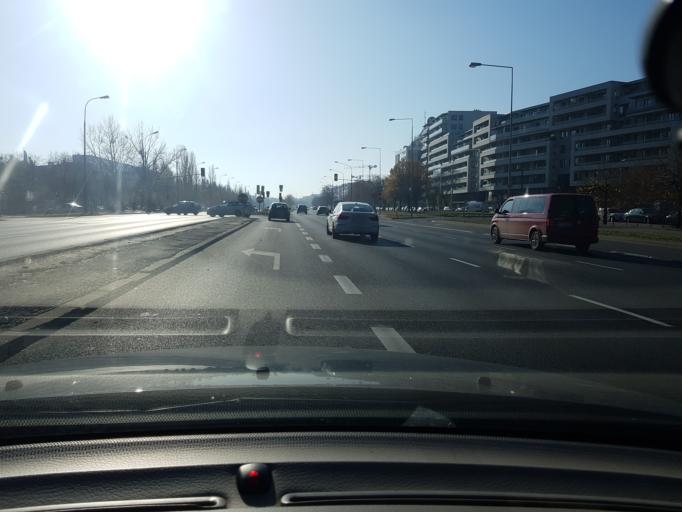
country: PL
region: Masovian Voivodeship
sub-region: Warszawa
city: Mokotow
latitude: 52.1837
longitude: 21.0455
